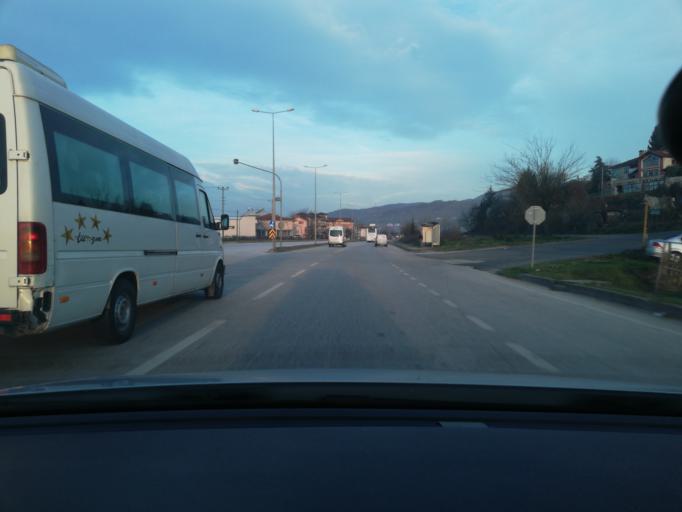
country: TR
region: Duzce
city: Konuralp
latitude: 40.9006
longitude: 31.1514
